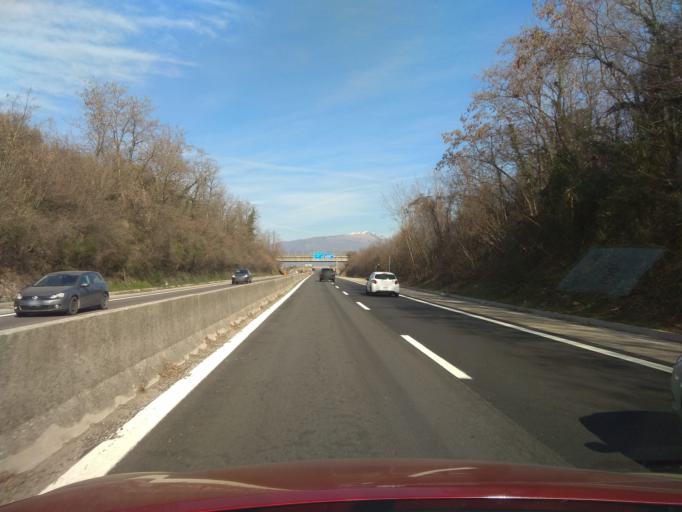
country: IT
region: Veneto
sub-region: Provincia di Verona
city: Calmasino
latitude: 45.5126
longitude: 10.7688
